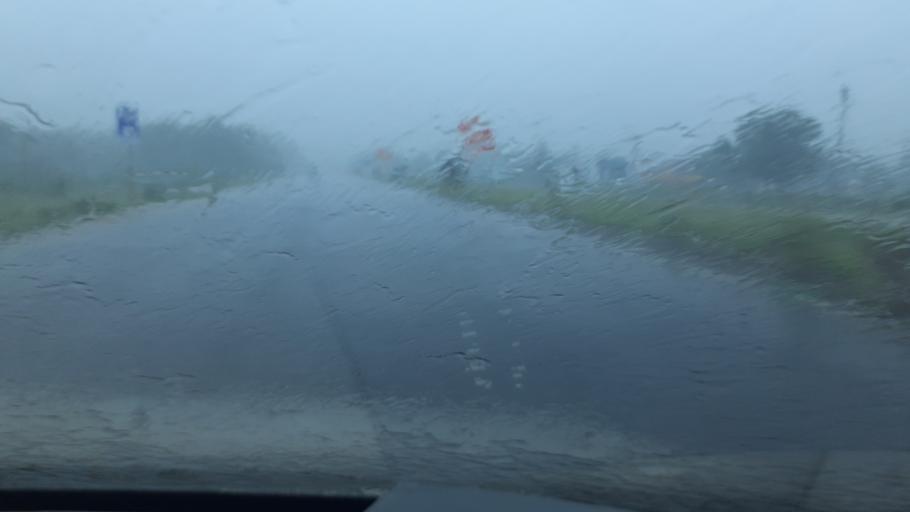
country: IN
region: Tamil Nadu
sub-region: Virudhunagar
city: Virudunagar
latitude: 9.4982
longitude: 77.9416
